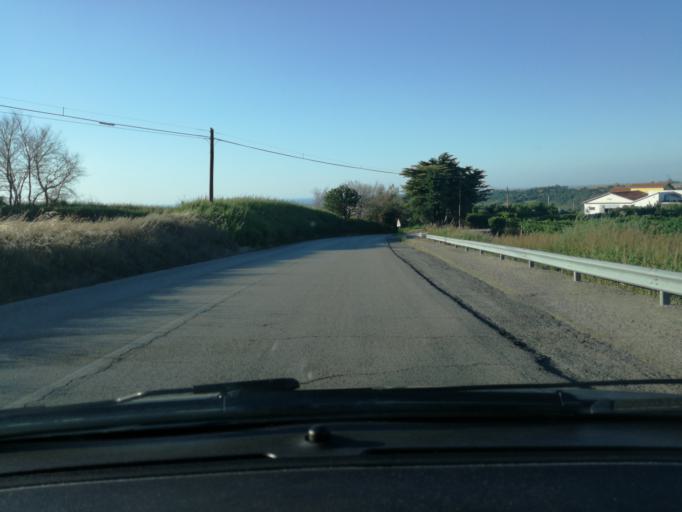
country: IT
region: Molise
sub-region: Provincia di Campobasso
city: Guglionesi
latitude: 41.9301
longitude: 14.9298
